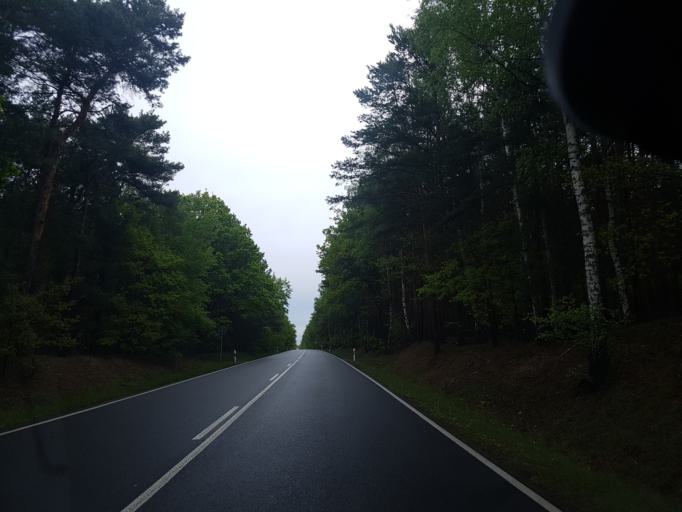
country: DE
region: Brandenburg
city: Neupetershain
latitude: 51.6138
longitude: 14.1445
